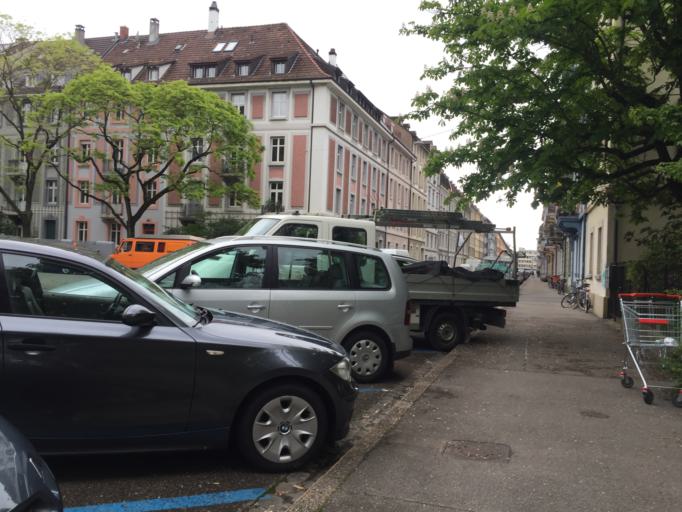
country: CH
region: Basel-Landschaft
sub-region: Bezirk Arlesheim
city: Birsfelden
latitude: 47.5438
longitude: 7.5976
